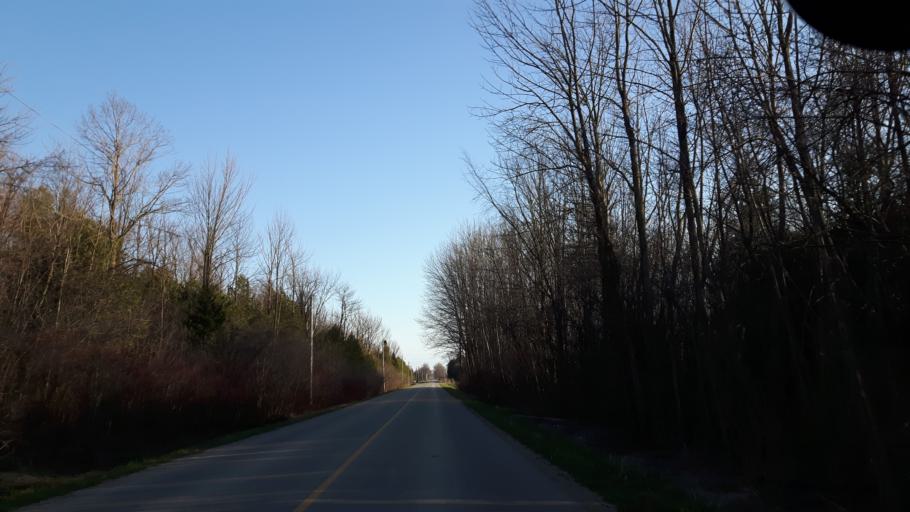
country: CA
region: Ontario
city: Goderich
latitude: 43.6886
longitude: -81.6848
